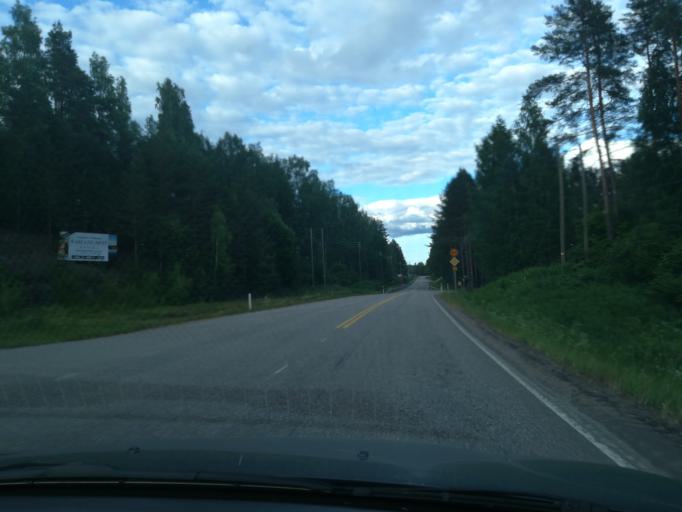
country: FI
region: Southern Savonia
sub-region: Mikkeli
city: Puumala
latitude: 61.5750
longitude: 28.1420
